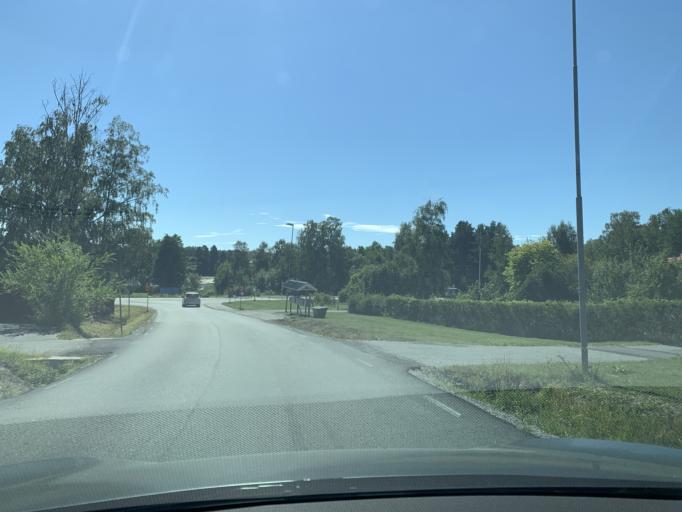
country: SE
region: Stockholm
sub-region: Botkyrka Kommun
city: Eriksberg
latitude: 59.2428
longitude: 17.7860
